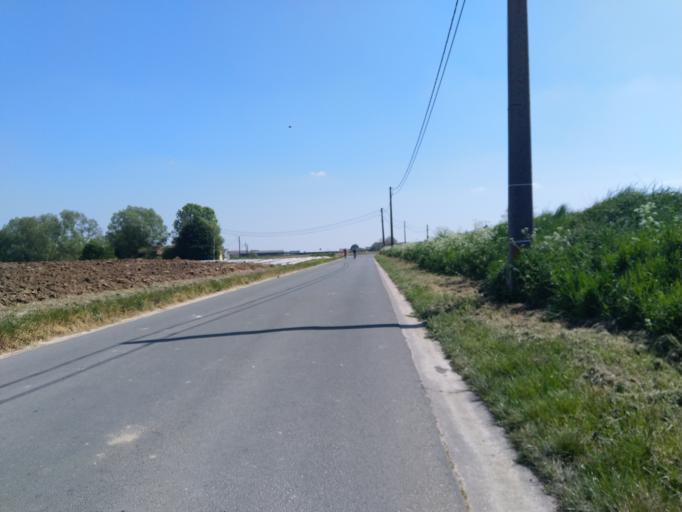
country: BE
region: Wallonia
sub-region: Province du Hainaut
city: Enghien
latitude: 50.6662
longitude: 4.0481
